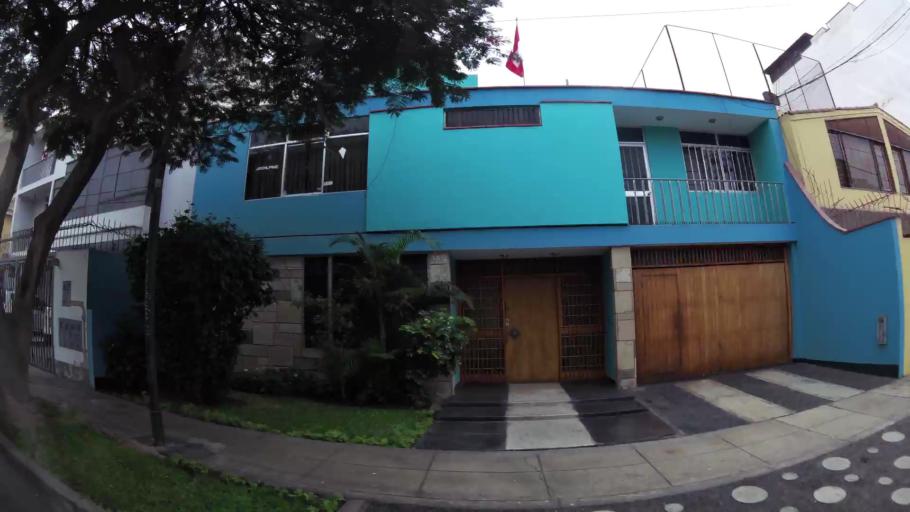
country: PE
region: Lima
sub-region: Lima
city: Surco
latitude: -12.1361
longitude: -76.9978
